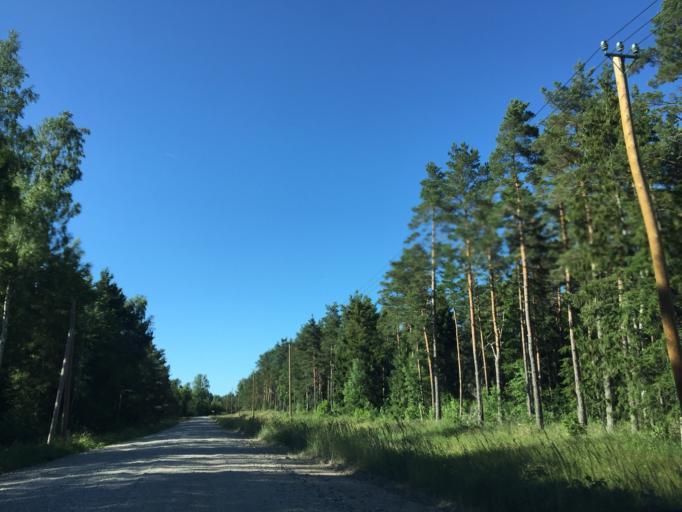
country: LV
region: Ventspils
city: Ventspils
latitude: 57.5670
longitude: 21.7232
